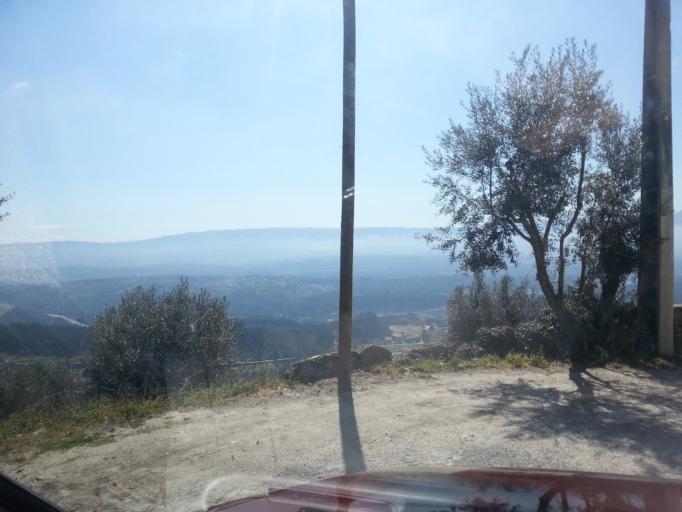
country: PT
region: Guarda
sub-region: Fornos de Algodres
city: Fornos de Algodres
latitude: 40.6292
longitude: -7.5381
